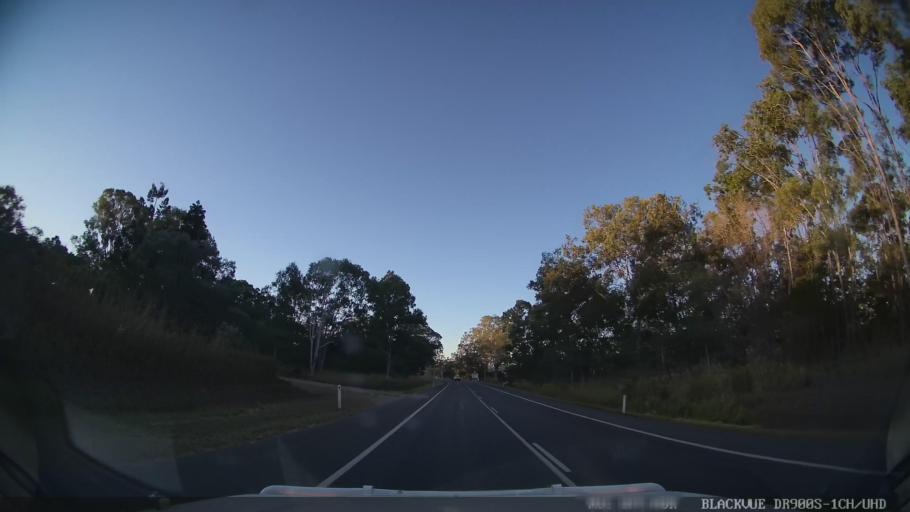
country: AU
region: Queensland
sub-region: Gladstone
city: Toolooa
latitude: -23.9574
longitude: 151.2196
